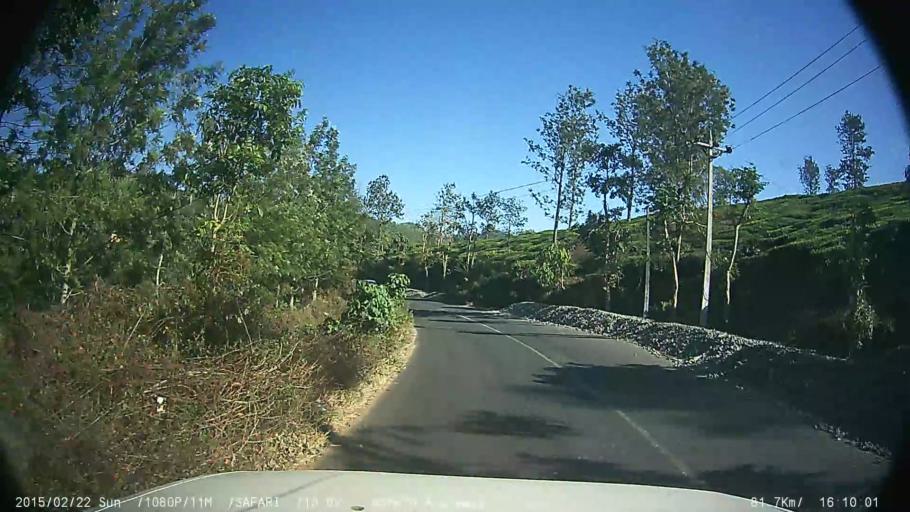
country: IN
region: Tamil Nadu
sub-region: Theni
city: Gudalur
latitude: 9.5713
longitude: 77.0840
